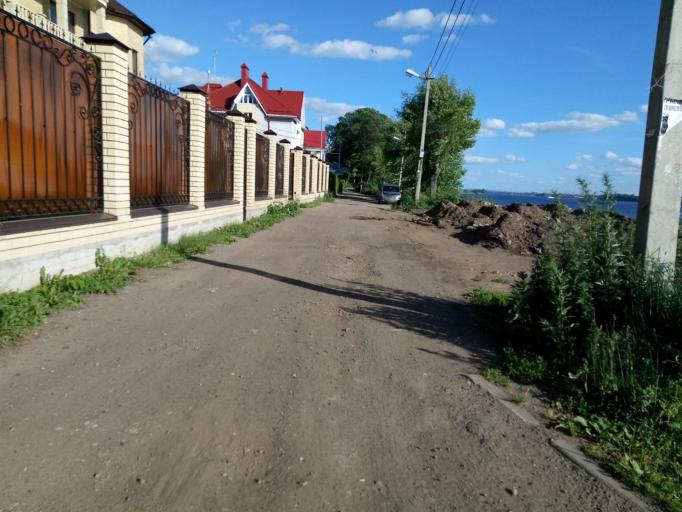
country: RU
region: Jaroslavl
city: Yaroslavl
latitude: 57.6343
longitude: 39.9052
